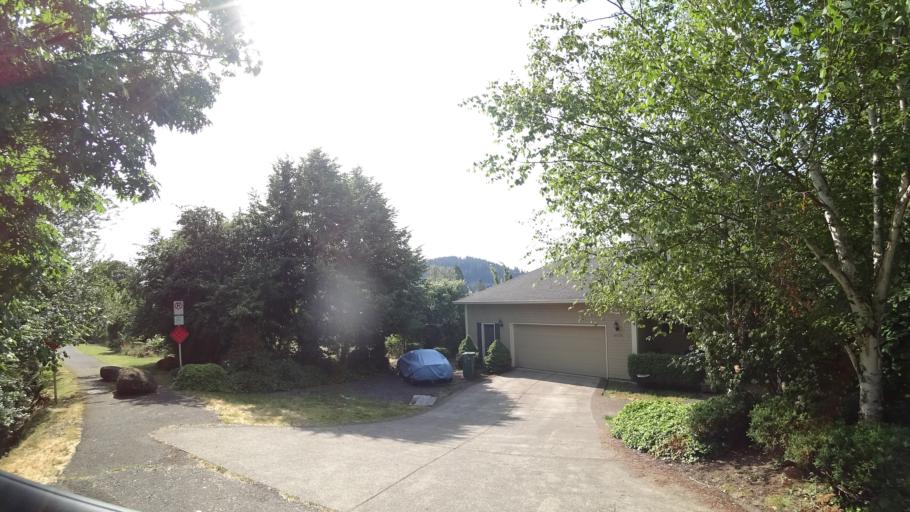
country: US
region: Oregon
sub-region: Clackamas County
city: Happy Valley
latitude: 45.4549
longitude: -122.5240
